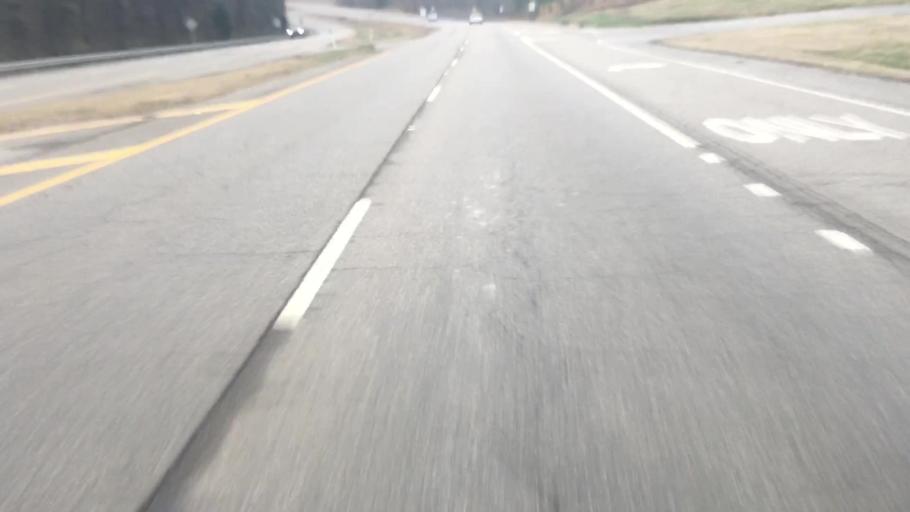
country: US
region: Alabama
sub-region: Walker County
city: Sumiton
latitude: 33.7506
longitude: -87.0584
